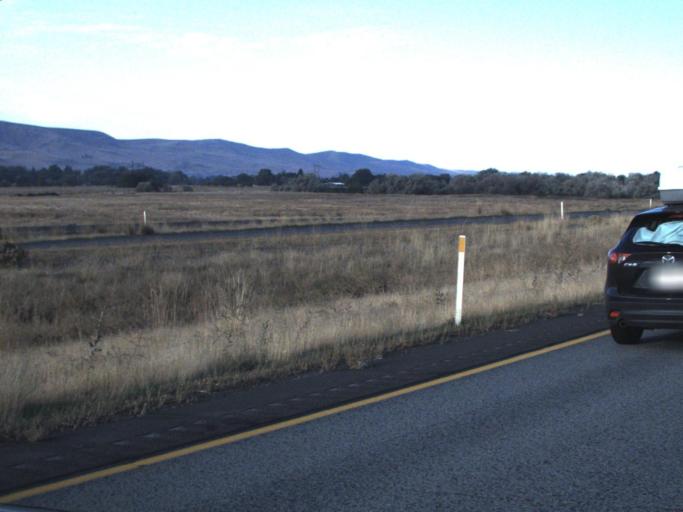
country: US
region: Washington
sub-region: Benton County
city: Prosser
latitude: 46.2213
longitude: -119.7566
